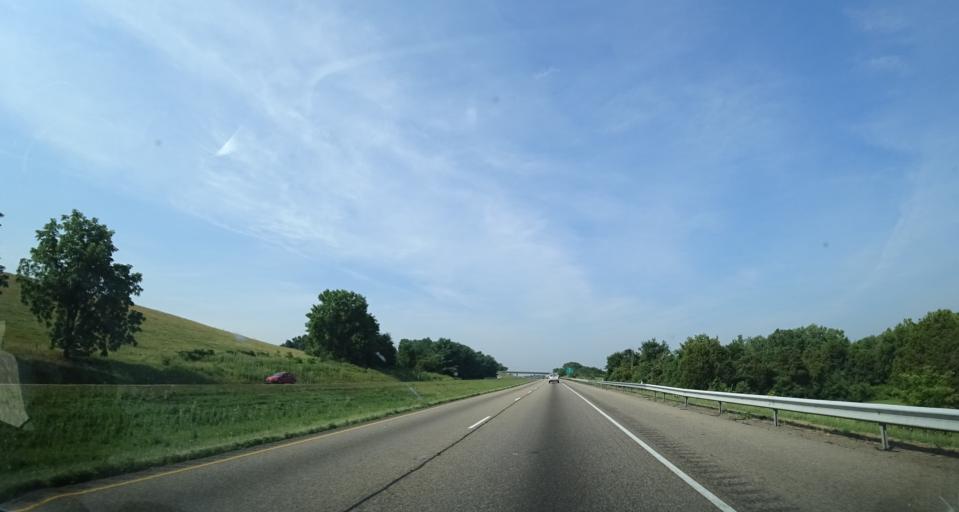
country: US
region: Virginia
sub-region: City of Harrisonburg
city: Harrisonburg
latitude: 38.4983
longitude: -78.7967
